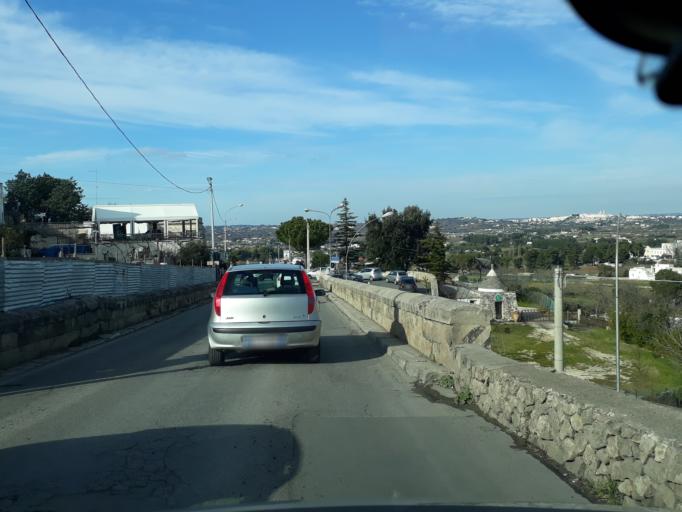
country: IT
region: Apulia
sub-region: Provincia di Taranto
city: Martina Franca
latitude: 40.7075
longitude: 17.3386
